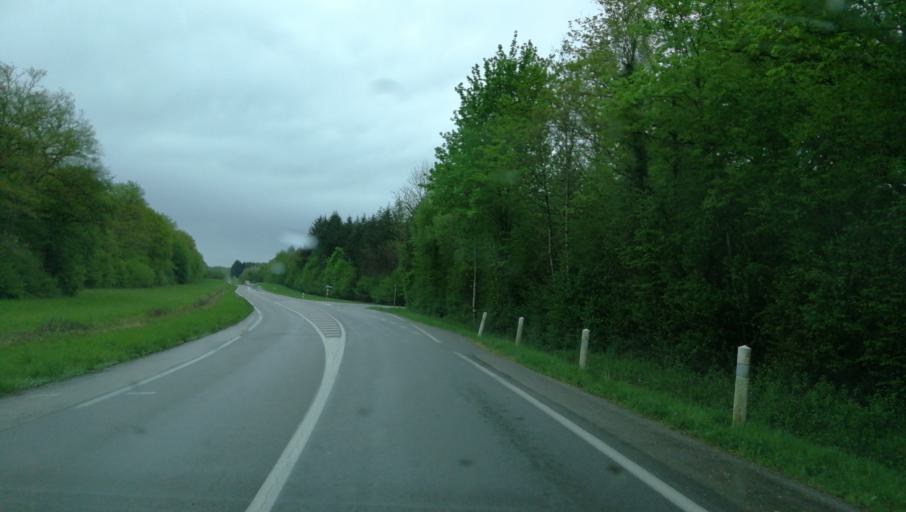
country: FR
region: Franche-Comte
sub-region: Departement du Jura
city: Montmorot
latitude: 46.7012
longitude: 5.4852
